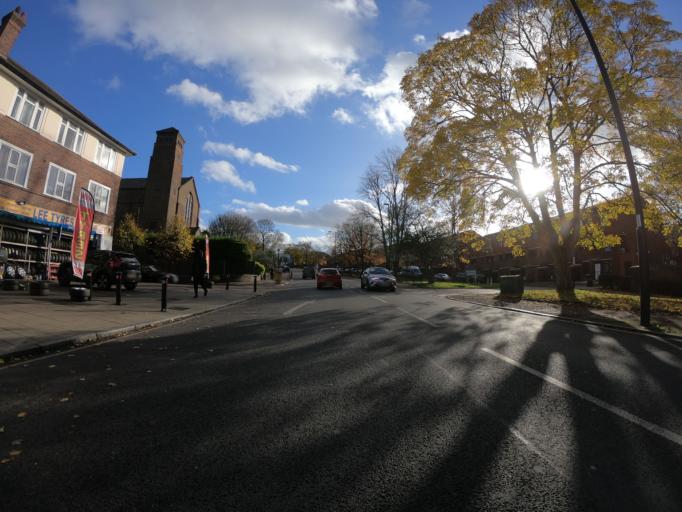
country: GB
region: England
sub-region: Greater London
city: Blackheath
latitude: 51.4481
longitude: 0.0134
